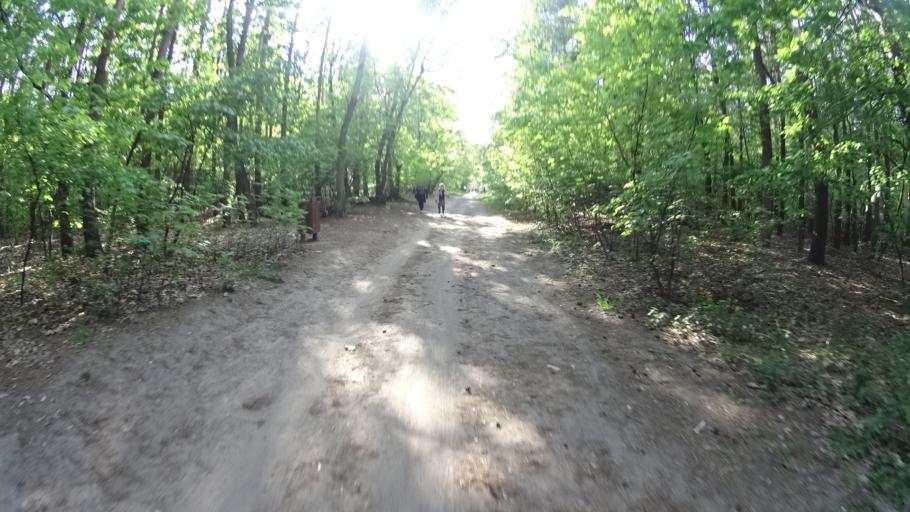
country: PL
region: Masovian Voivodeship
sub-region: Powiat warszawski zachodni
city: Babice
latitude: 52.2534
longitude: 20.8701
